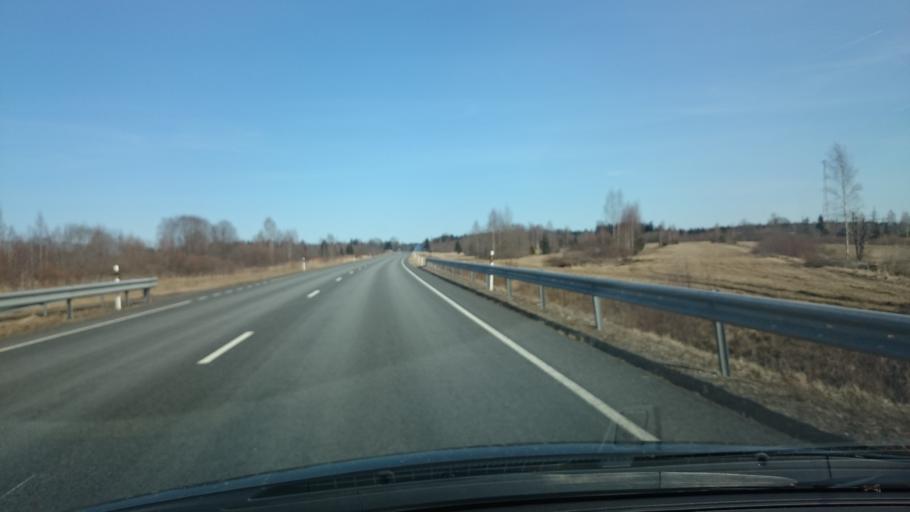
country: EE
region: Paernumaa
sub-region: Vaendra vald (alev)
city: Vandra
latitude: 58.6593
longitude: 25.0124
